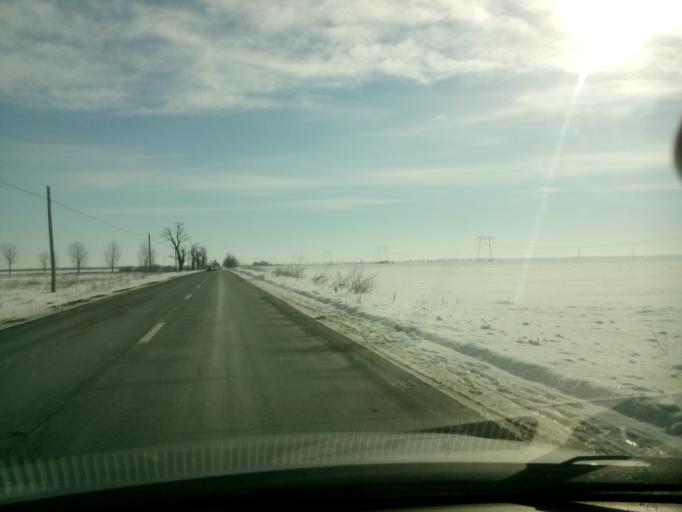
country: RO
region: Calarasi
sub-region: Comuna Frumusani
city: Frumusani
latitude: 44.2703
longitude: 26.3449
